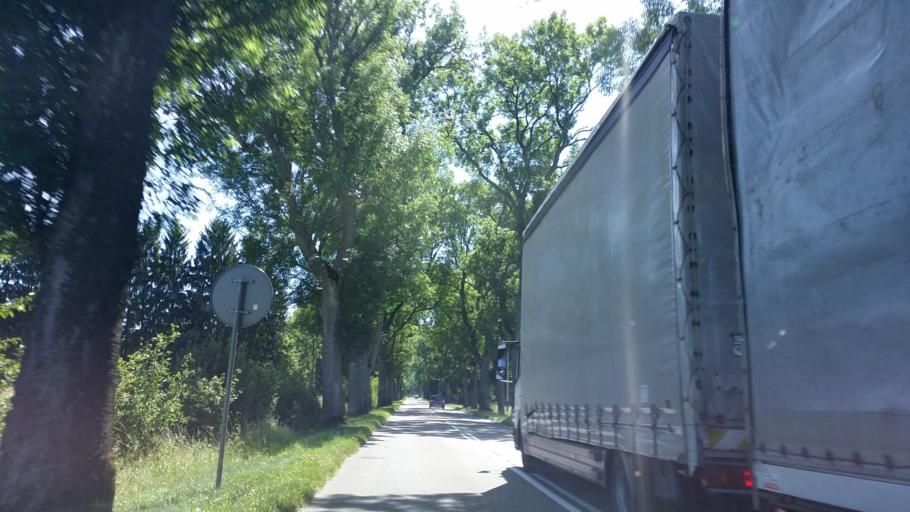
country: PL
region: West Pomeranian Voivodeship
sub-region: Powiat lobeski
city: Lobez
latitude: 53.6207
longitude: 15.6121
